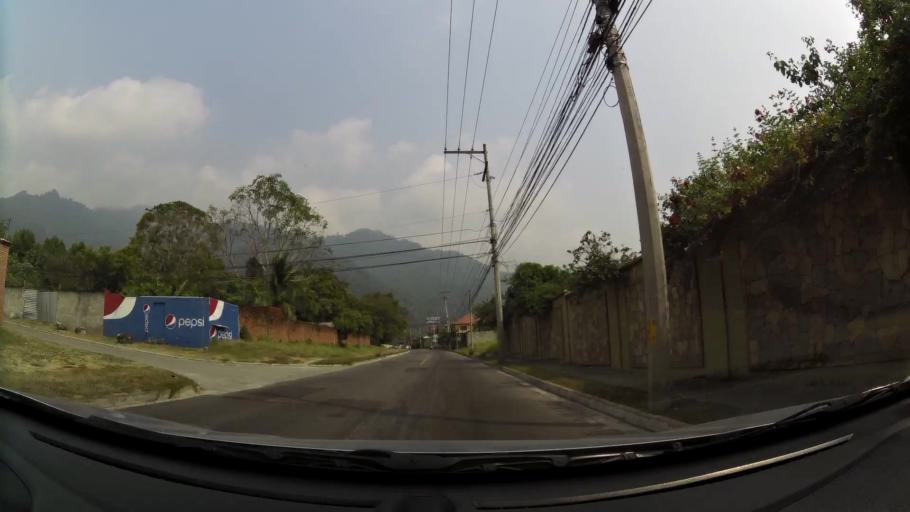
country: HN
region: Cortes
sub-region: San Pedro Sula
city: Pena Blanca
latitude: 15.5481
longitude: -88.0351
